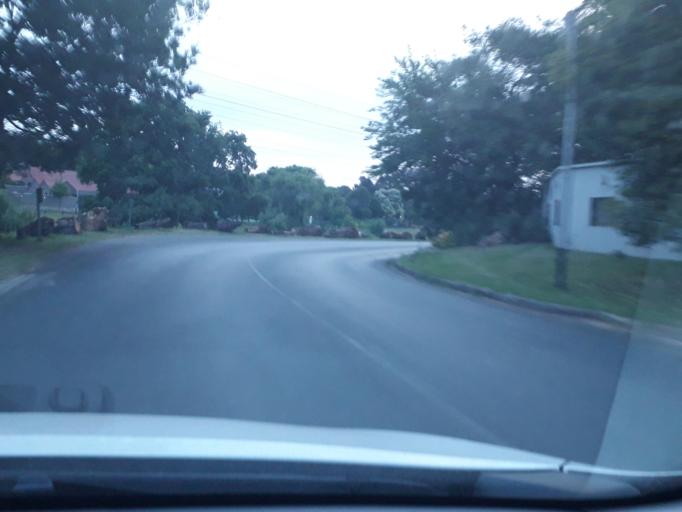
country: ZA
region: Gauteng
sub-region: City of Johannesburg Metropolitan Municipality
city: Johannesburg
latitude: -26.1489
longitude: 27.9975
